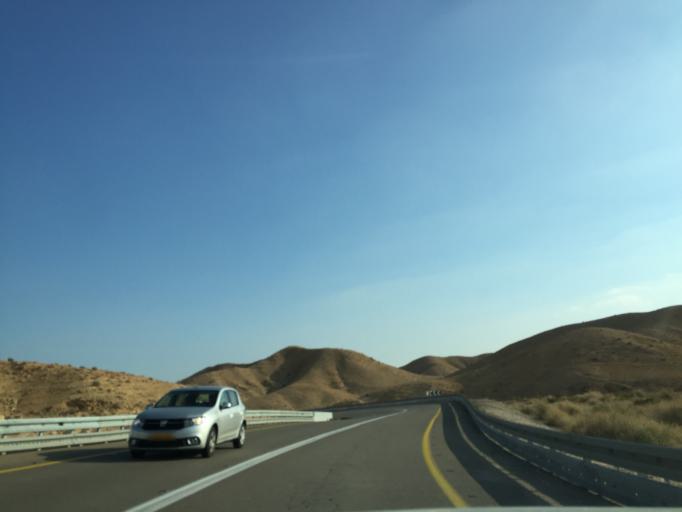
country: IL
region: Southern District
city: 'Arad
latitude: 31.1975
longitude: 35.2701
